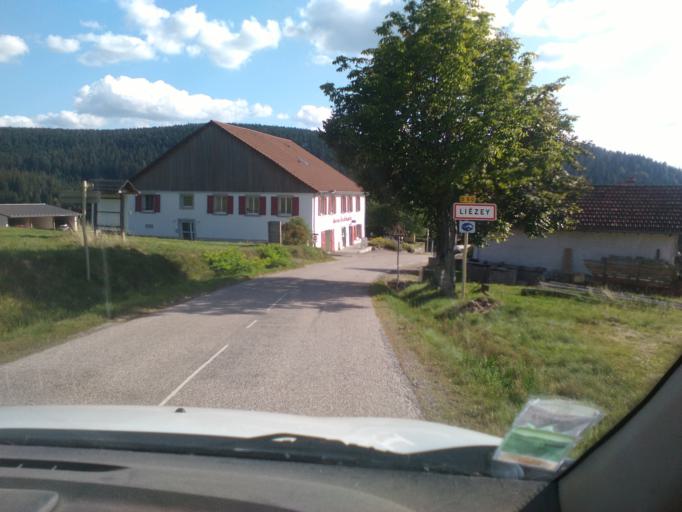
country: FR
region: Lorraine
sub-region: Departement des Vosges
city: Granges-sur-Vologne
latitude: 48.0951
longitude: 6.8052
